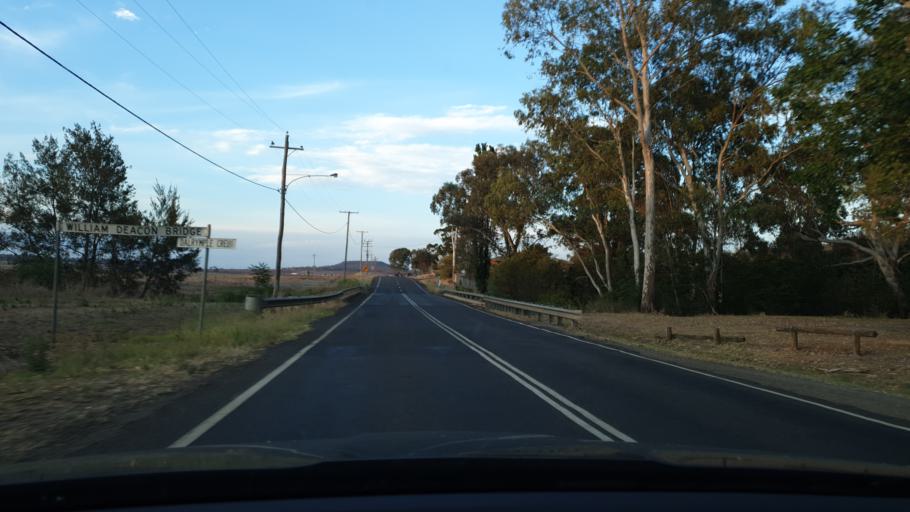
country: AU
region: Queensland
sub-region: Southern Downs
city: Warwick
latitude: -28.0286
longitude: 151.9828
